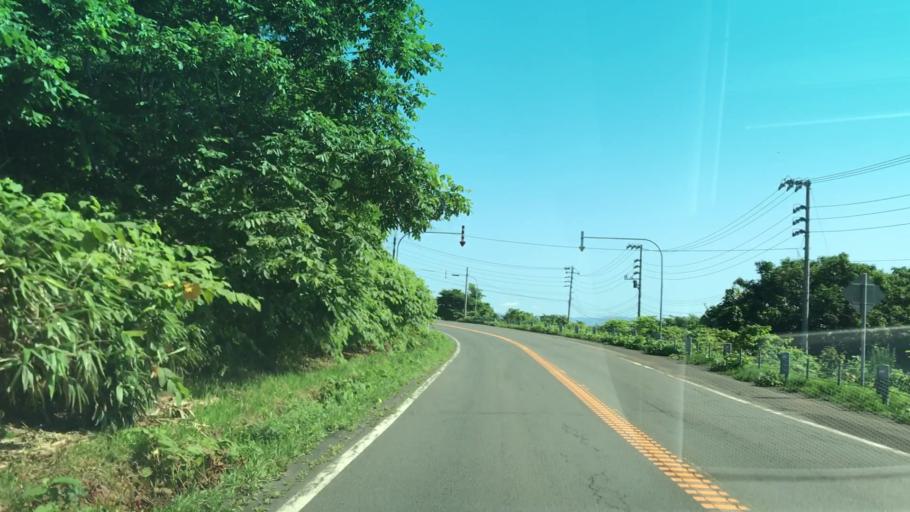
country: JP
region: Hokkaido
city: Iwanai
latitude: 43.1366
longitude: 140.4299
